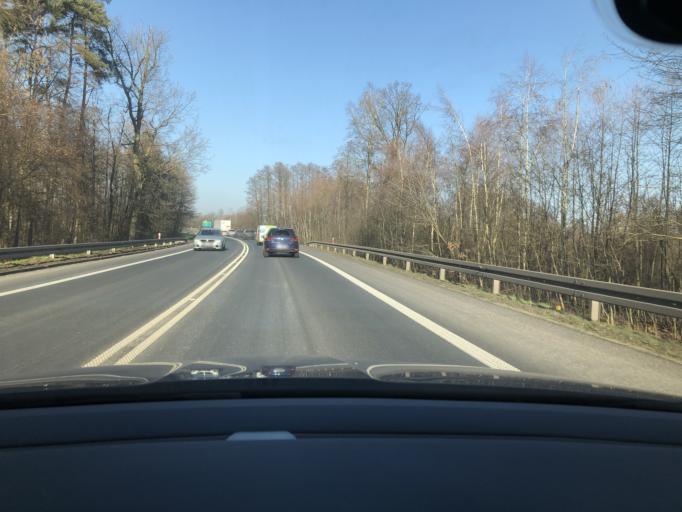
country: PL
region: Greater Poland Voivodeship
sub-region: Powiat szamotulski
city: Pniewy
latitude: 52.5125
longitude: 16.2323
